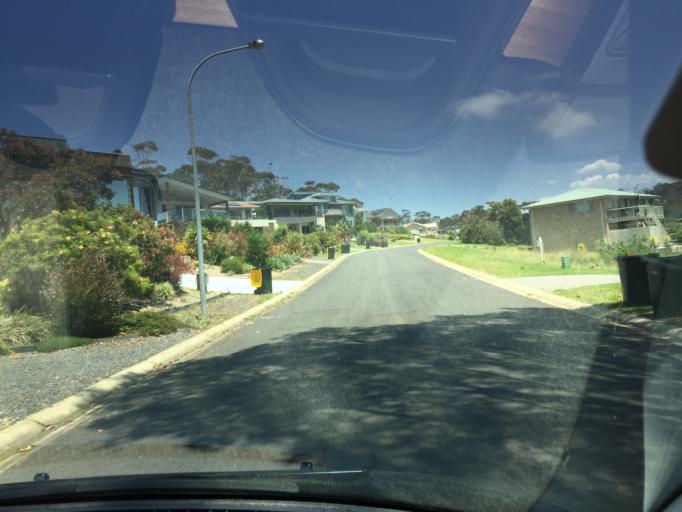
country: AU
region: New South Wales
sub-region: Bega Valley
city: Merimbula
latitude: -36.8496
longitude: 149.9338
